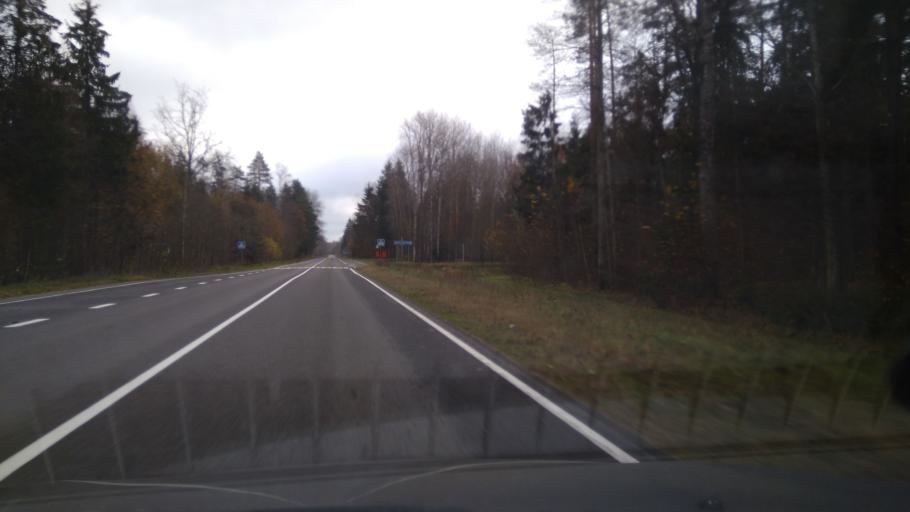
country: BY
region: Minsk
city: Urechcha
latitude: 53.2097
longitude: 27.9003
